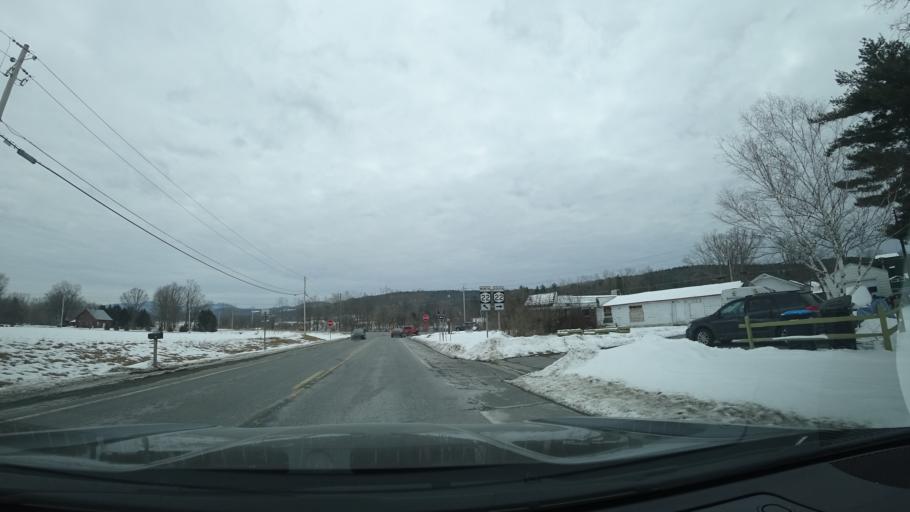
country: US
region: New York
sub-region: Washington County
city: Cambridge
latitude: 43.1501
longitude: -73.3553
